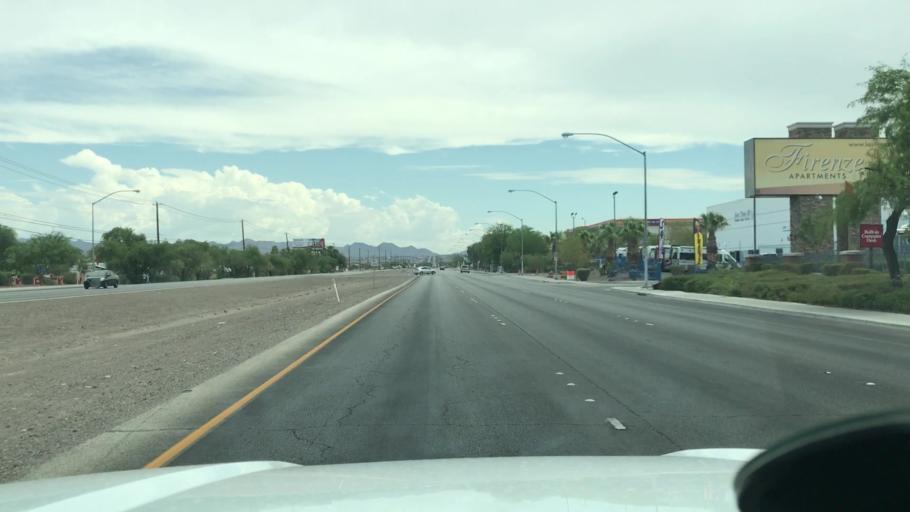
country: US
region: Nevada
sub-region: Clark County
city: Whitney
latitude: 36.0822
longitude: -115.0302
